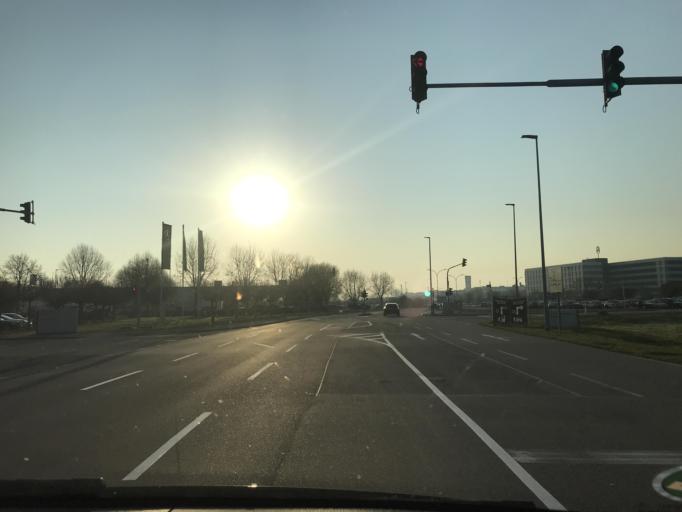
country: DE
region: Rheinland-Pfalz
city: Worth am Rhein
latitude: 49.0520
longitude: 8.2782
